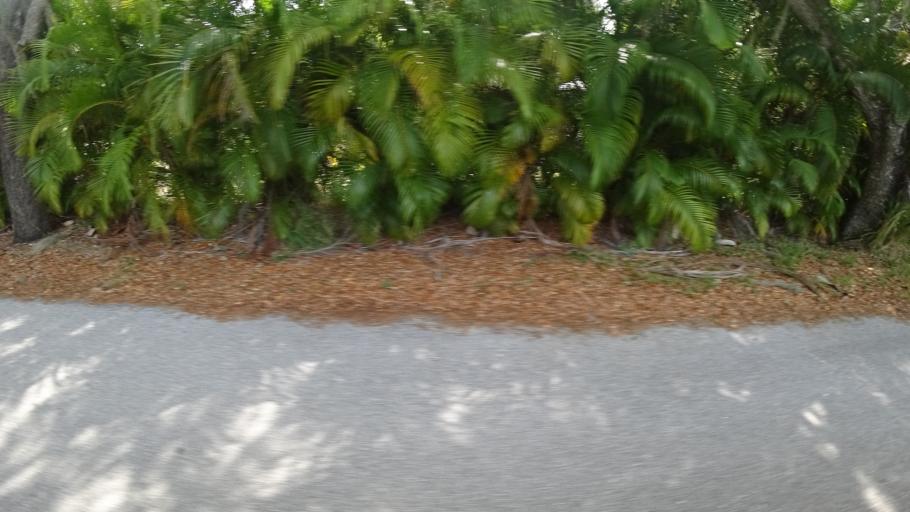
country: US
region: Florida
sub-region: Sarasota County
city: North Sarasota
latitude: 27.4005
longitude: -82.5301
